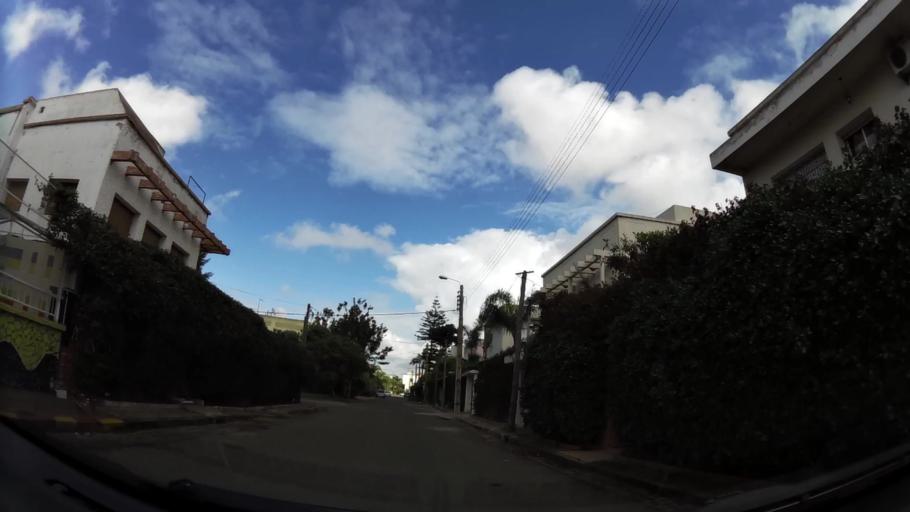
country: MA
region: Grand Casablanca
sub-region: Casablanca
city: Casablanca
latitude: 33.5515
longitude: -7.6260
